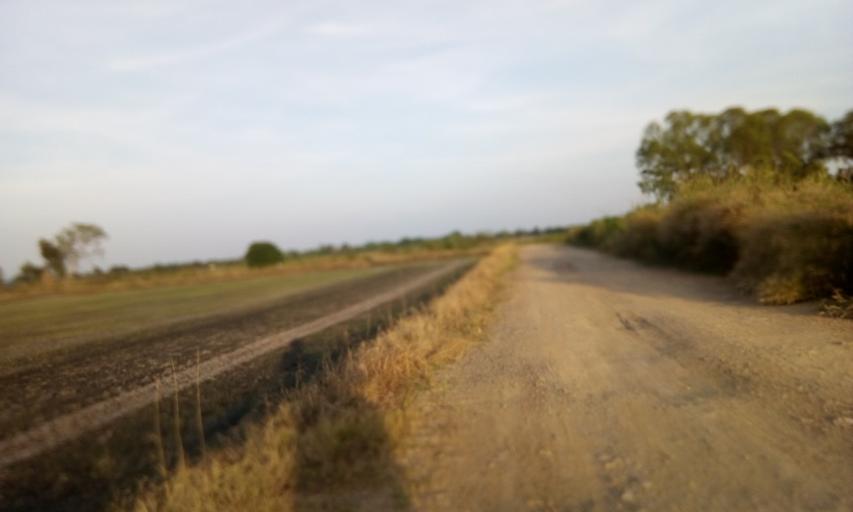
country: TH
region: Pathum Thani
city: Ban Lam Luk Ka
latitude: 14.0351
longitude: 100.8558
